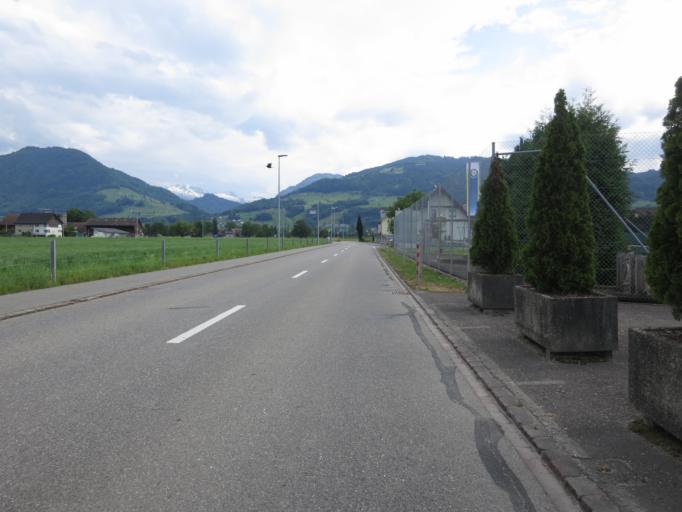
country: CH
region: Schwyz
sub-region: Bezirk March
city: Lachen
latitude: 47.1933
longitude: 8.8827
